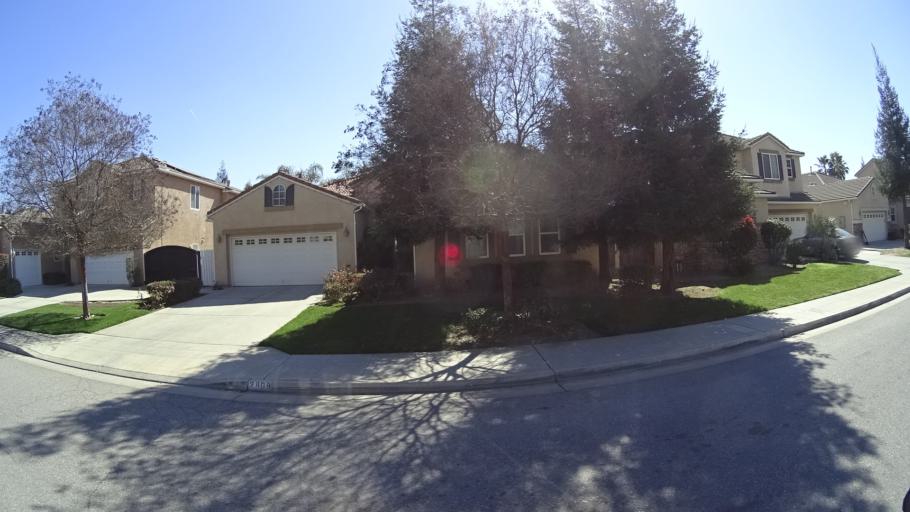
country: US
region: California
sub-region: Fresno County
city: Clovis
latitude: 36.8552
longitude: -119.7327
